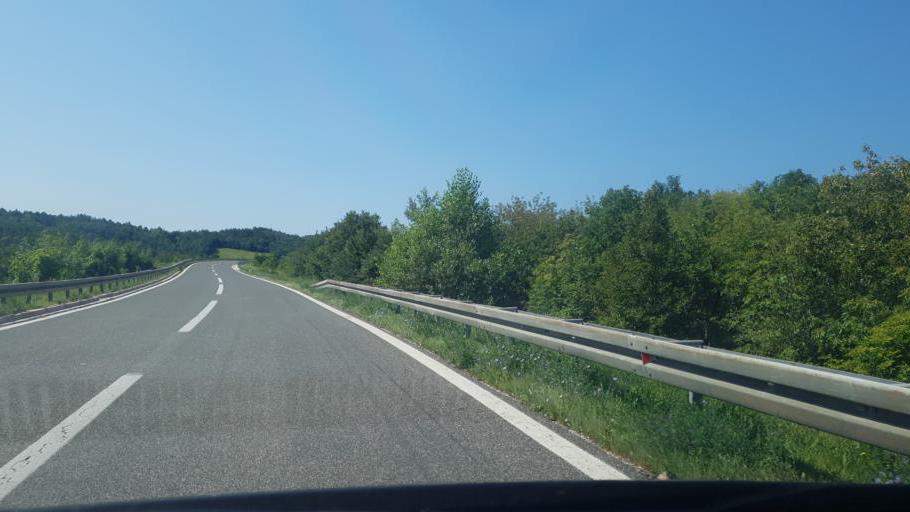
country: HR
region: Istarska
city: Buzet
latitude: 45.3483
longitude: 14.0837
